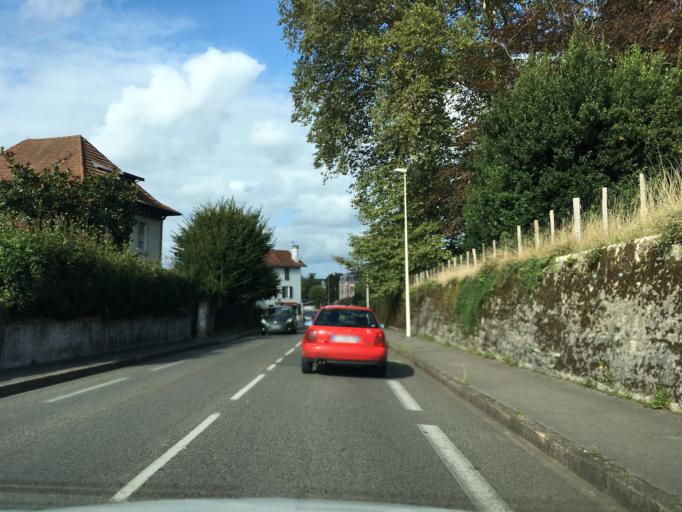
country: FR
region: Aquitaine
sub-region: Departement des Pyrenees-Atlantiques
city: Bayonne
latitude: 43.4800
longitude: -1.4838
